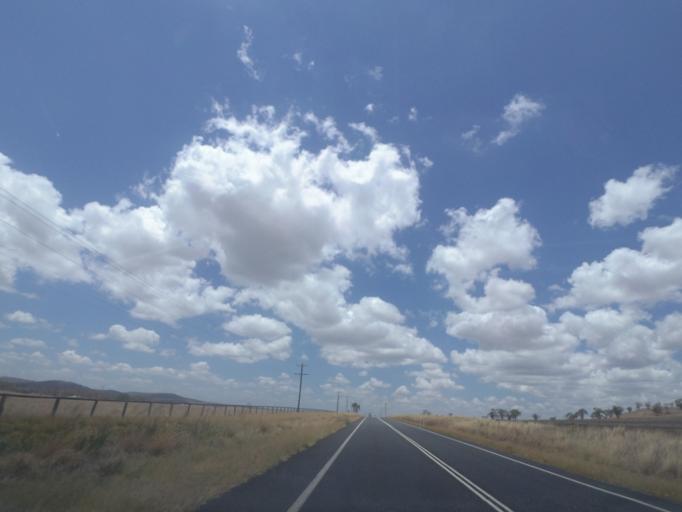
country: AU
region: Queensland
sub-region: Toowoomba
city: Top Camp
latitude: -27.7463
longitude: 151.9286
